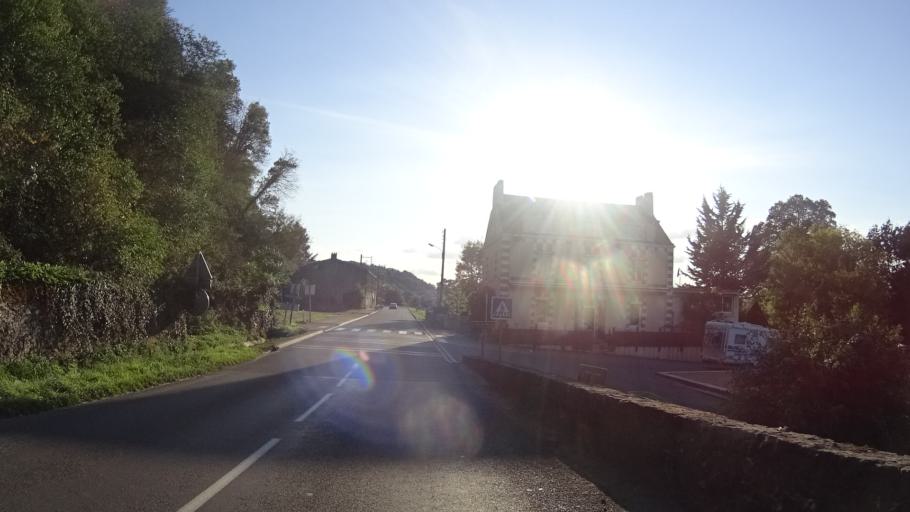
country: FR
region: Pays de la Loire
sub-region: Departement de Maine-et-Loire
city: Champtoceaux
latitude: 47.3390
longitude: -1.2743
